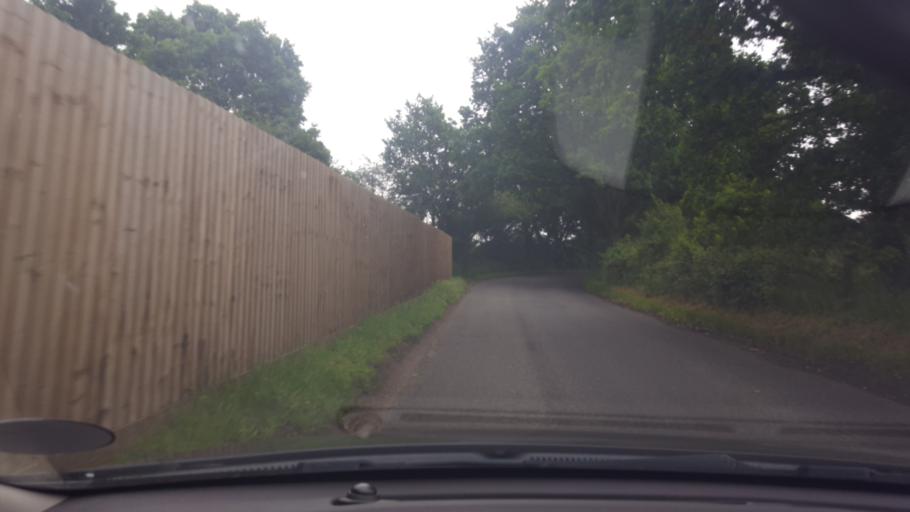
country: GB
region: England
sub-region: Essex
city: Great Bentley
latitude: 51.8728
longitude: 1.0800
